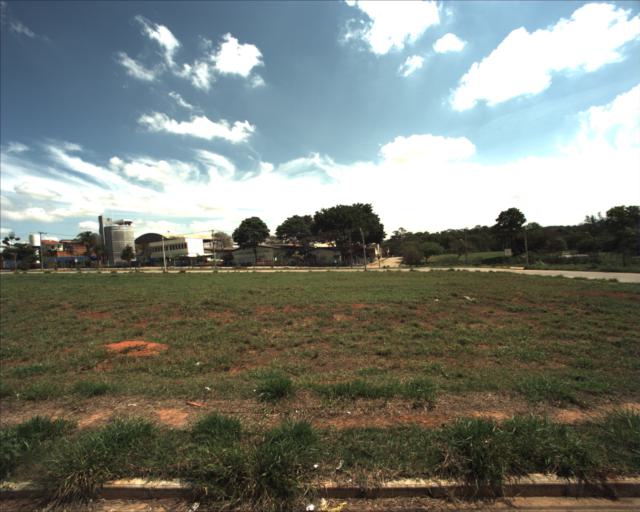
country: BR
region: Sao Paulo
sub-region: Sorocaba
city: Sorocaba
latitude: -23.4094
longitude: -47.4139
